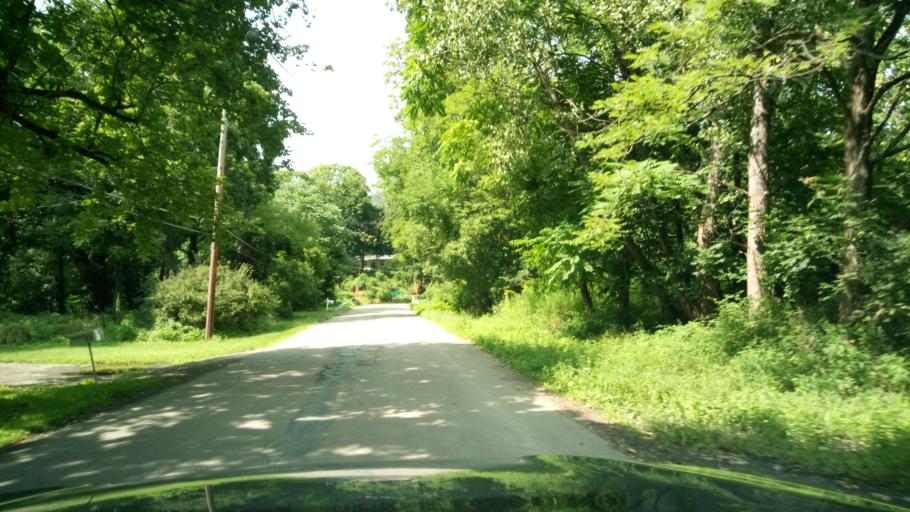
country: US
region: New York
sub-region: Chemung County
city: West Elmira
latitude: 42.0821
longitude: -76.8697
